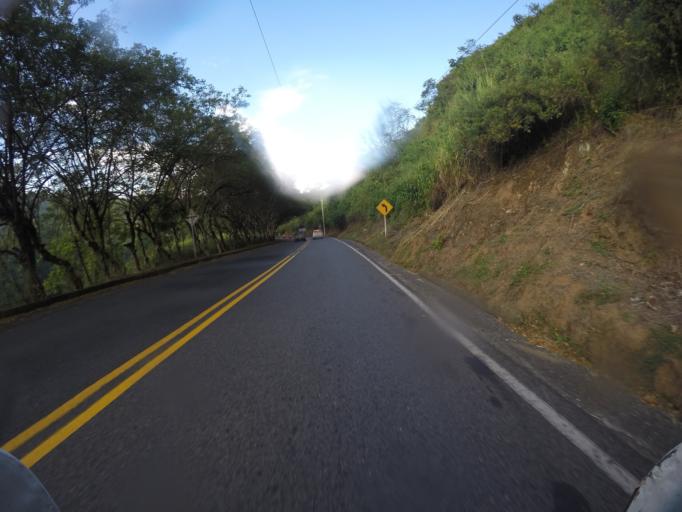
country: CO
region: Valle del Cauca
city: Cartago
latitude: 4.7288
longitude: -75.8705
